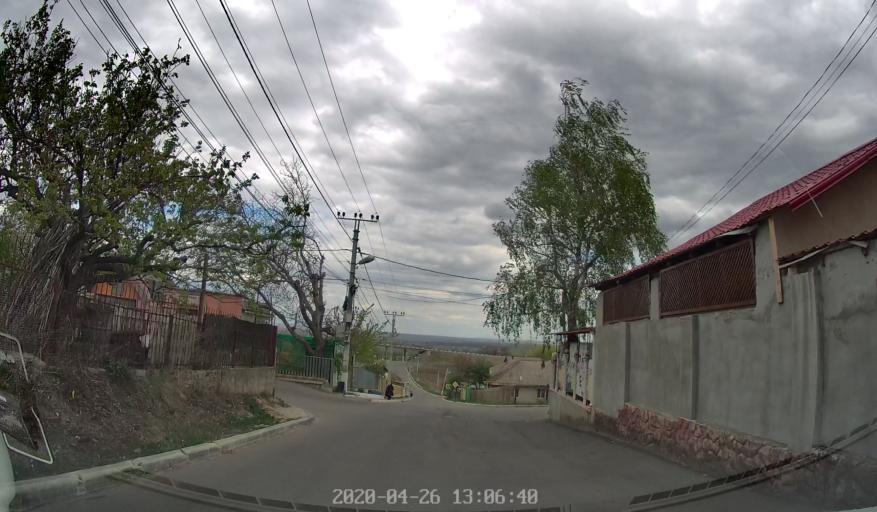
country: MD
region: Chisinau
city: Vadul lui Voda
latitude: 47.0829
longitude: 29.0743
